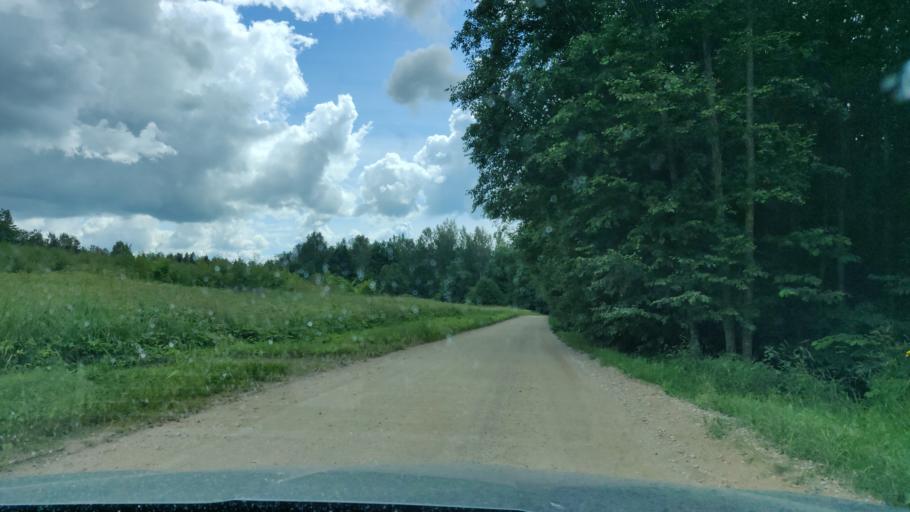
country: EE
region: Vorumaa
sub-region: Antsla vald
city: Vana-Antsla
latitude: 58.0366
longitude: 26.5542
